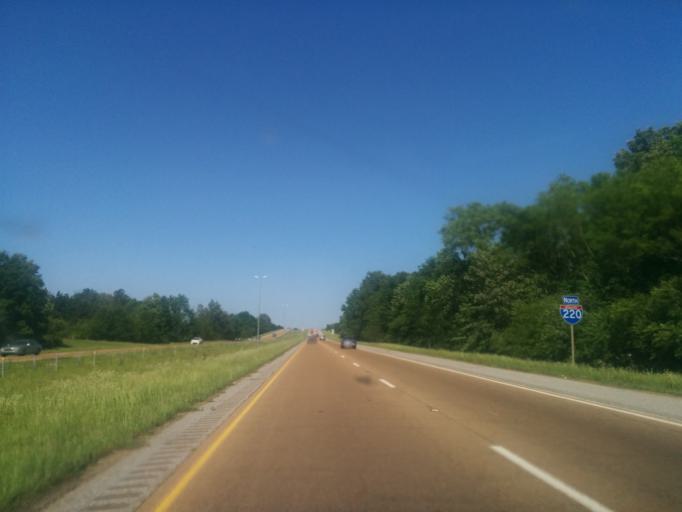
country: US
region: Mississippi
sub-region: Hinds County
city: Jackson
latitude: 32.3646
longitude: -90.2282
